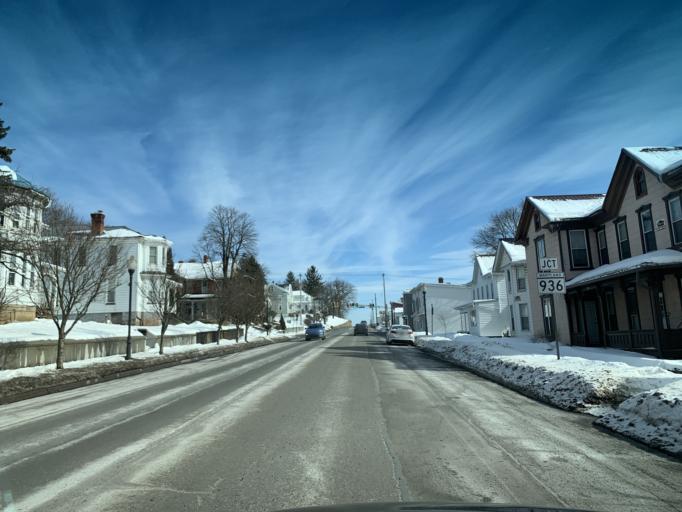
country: US
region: Maryland
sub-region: Allegany County
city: Frostburg
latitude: 39.6549
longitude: -78.9226
